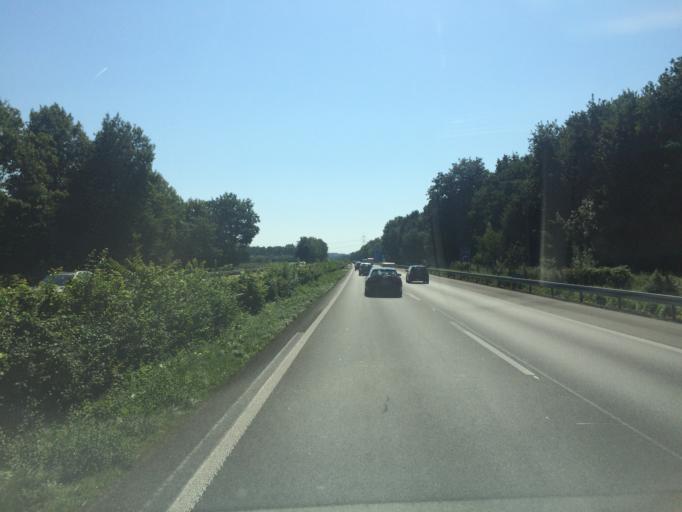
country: DE
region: North Rhine-Westphalia
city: Werne
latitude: 51.7043
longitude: 7.6621
